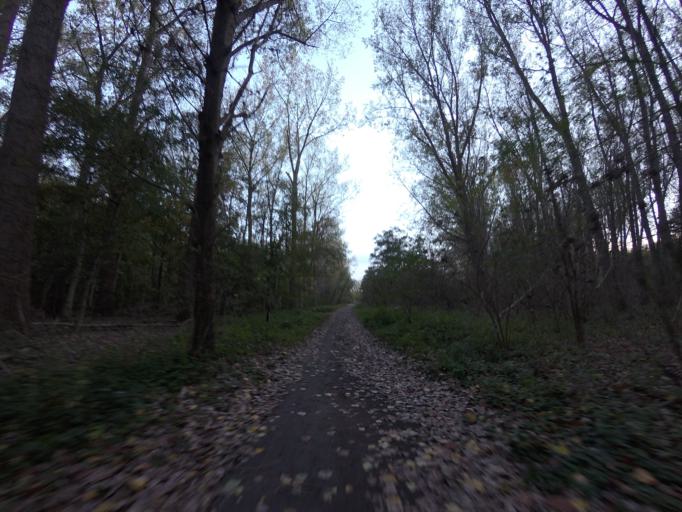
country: BE
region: Flanders
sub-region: Provincie Antwerpen
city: Zwijndrecht
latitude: 51.2316
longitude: 4.3632
